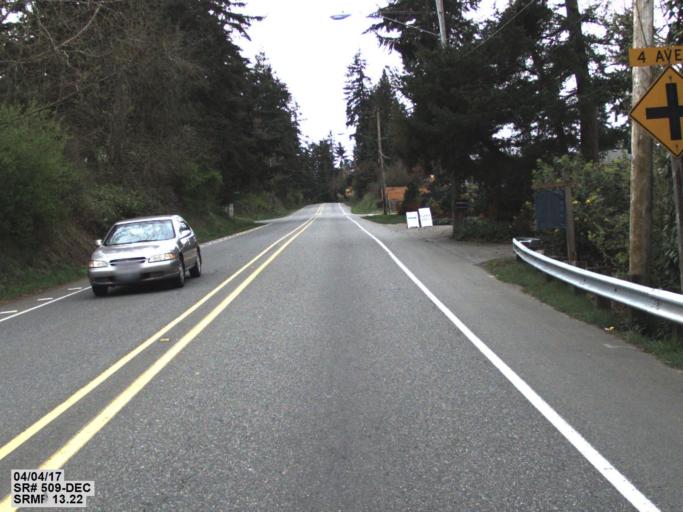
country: US
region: Washington
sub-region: King County
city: Federal Way
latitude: 47.3317
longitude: -122.3281
